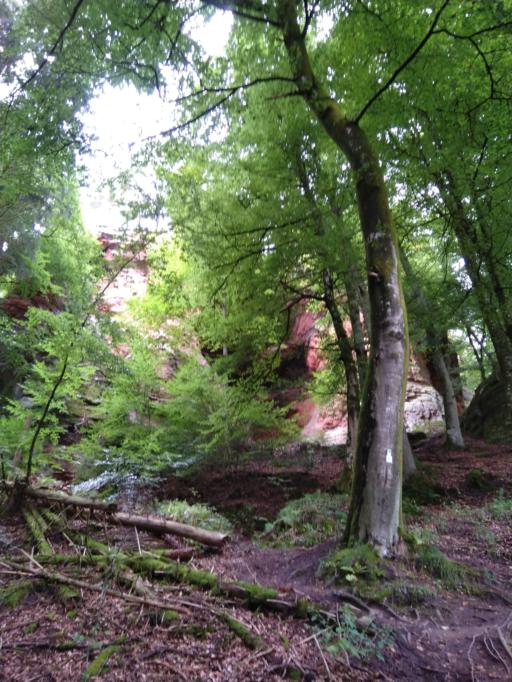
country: DE
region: Rheinland-Pfalz
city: Kordel
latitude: 49.8064
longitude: 6.6470
